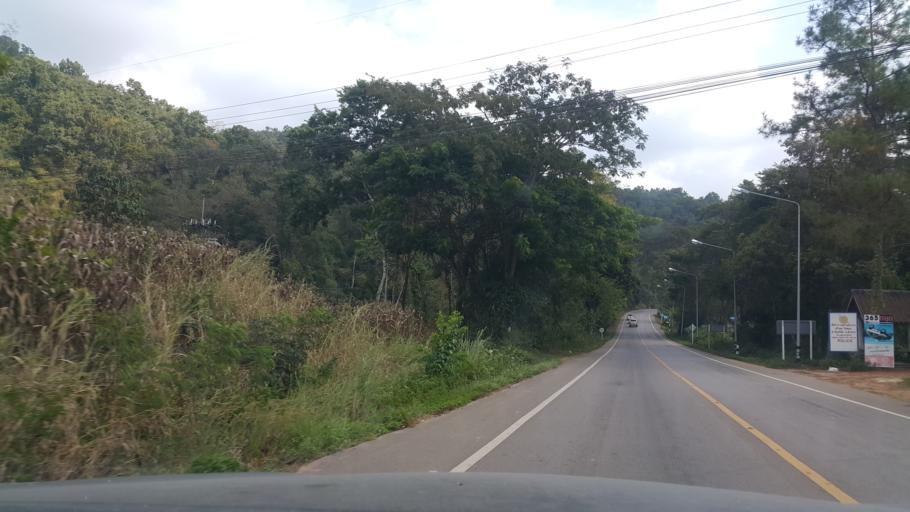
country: TH
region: Lampang
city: Wang Nuea
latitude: 19.0782
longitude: 99.7157
